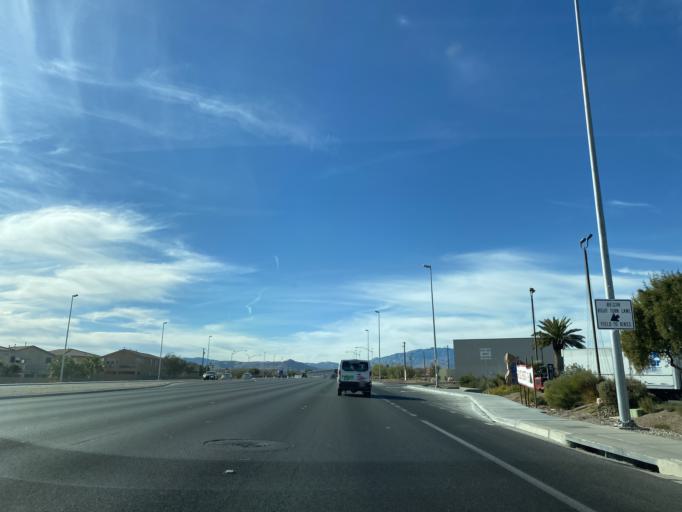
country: US
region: Nevada
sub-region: Clark County
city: Enterprise
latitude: 36.0297
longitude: -115.2148
